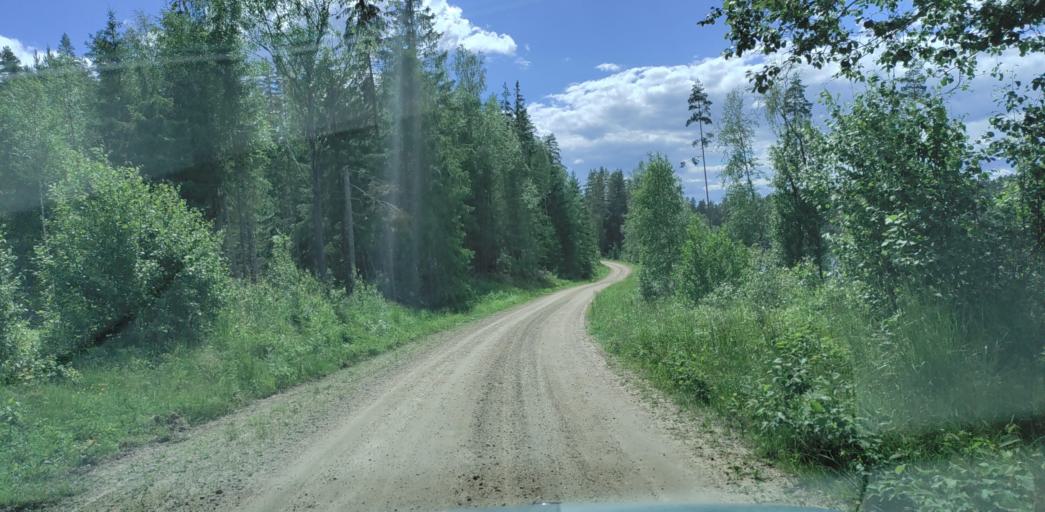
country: SE
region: Vaermland
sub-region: Hagfors Kommun
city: Ekshaerad
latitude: 60.0938
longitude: 13.3166
